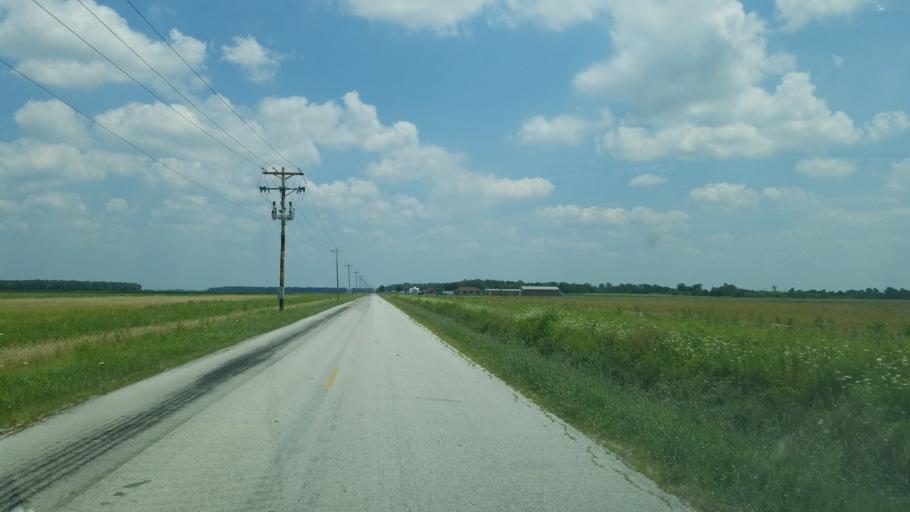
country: US
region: Ohio
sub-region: Wood County
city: North Baltimore
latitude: 41.2410
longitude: -83.7257
